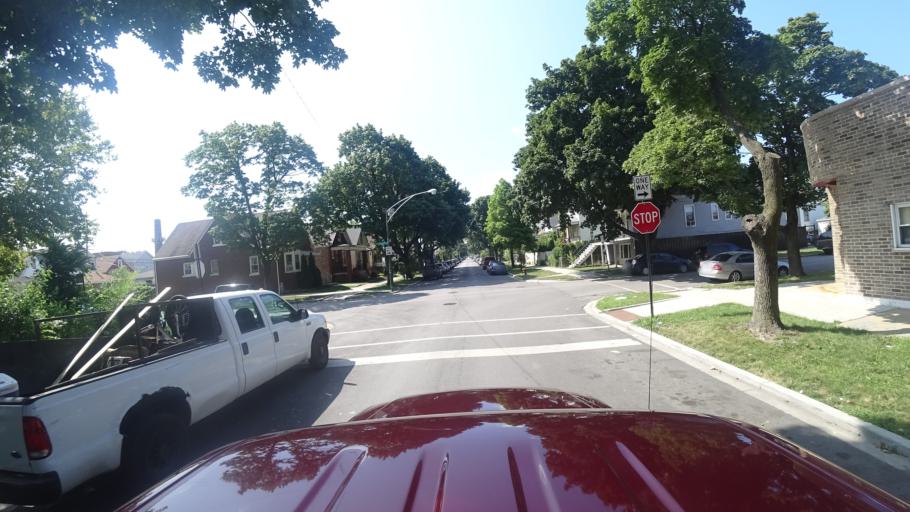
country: US
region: Illinois
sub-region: Cook County
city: Chicago
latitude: 41.7995
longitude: -87.6915
